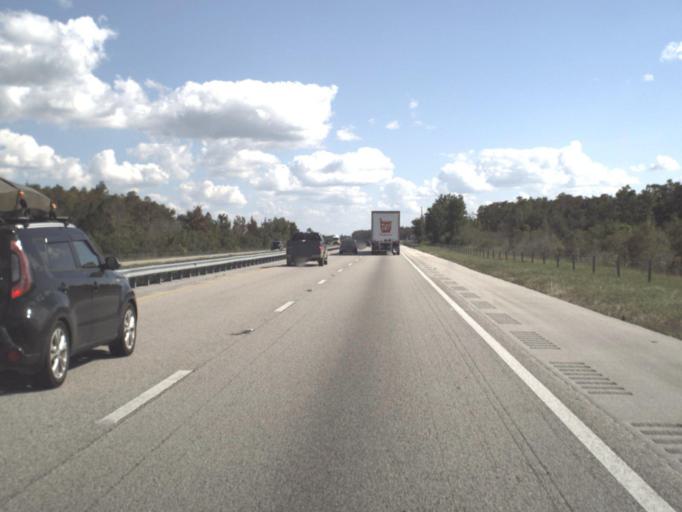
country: US
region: Florida
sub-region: Osceola County
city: Saint Cloud
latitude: 27.9752
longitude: -81.1137
